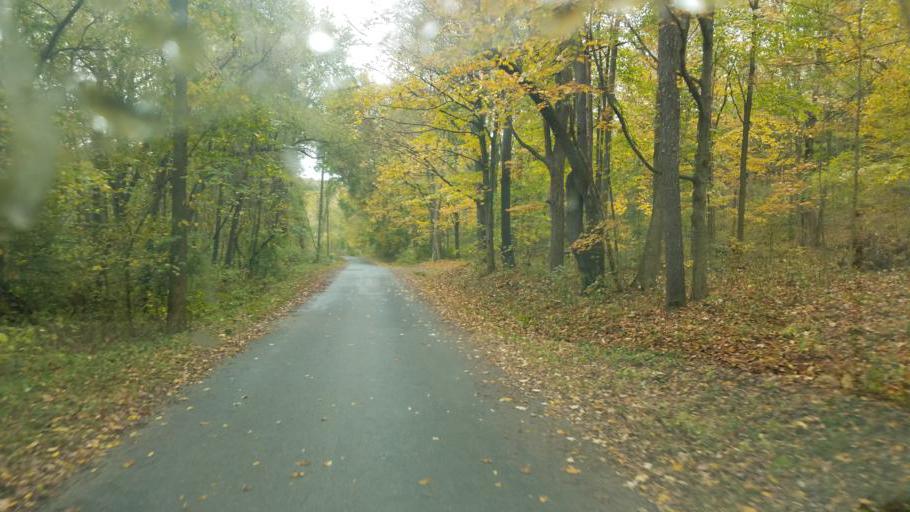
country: US
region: Ohio
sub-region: Holmes County
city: Millersburg
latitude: 40.5780
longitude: -81.8707
